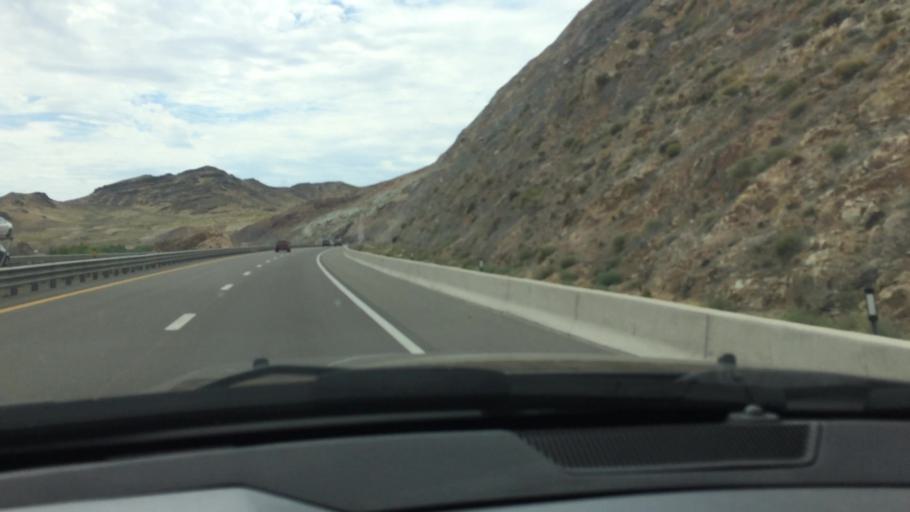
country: US
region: Nevada
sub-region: Lyon County
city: Fernley
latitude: 39.5983
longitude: -119.3527
